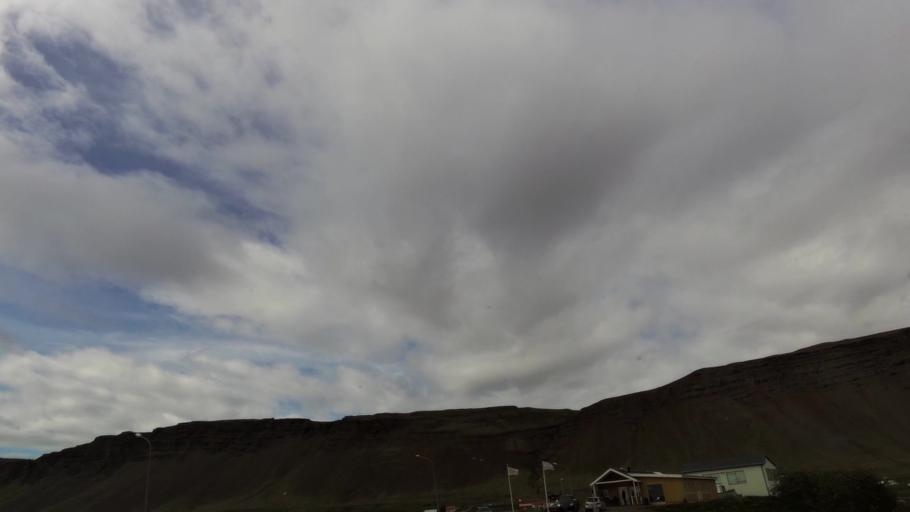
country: IS
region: West
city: Stykkisholmur
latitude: 65.4508
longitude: -22.2016
